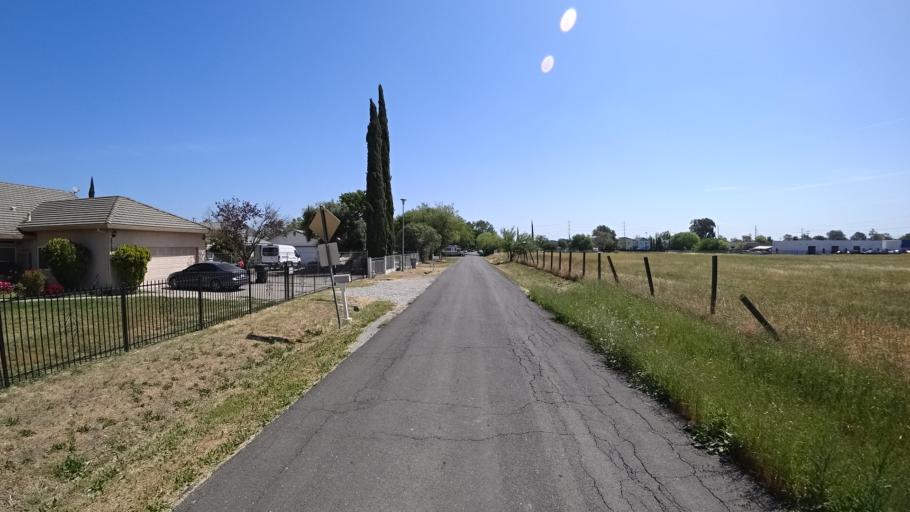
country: US
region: California
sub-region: Sacramento County
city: Parkway
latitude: 38.4977
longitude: -121.4766
